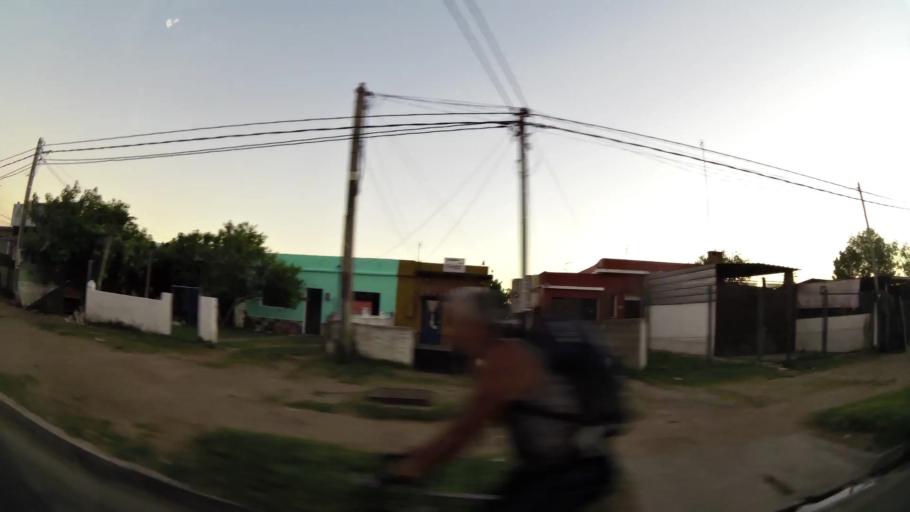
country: UY
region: Canelones
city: Toledo
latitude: -34.8174
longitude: -56.1419
